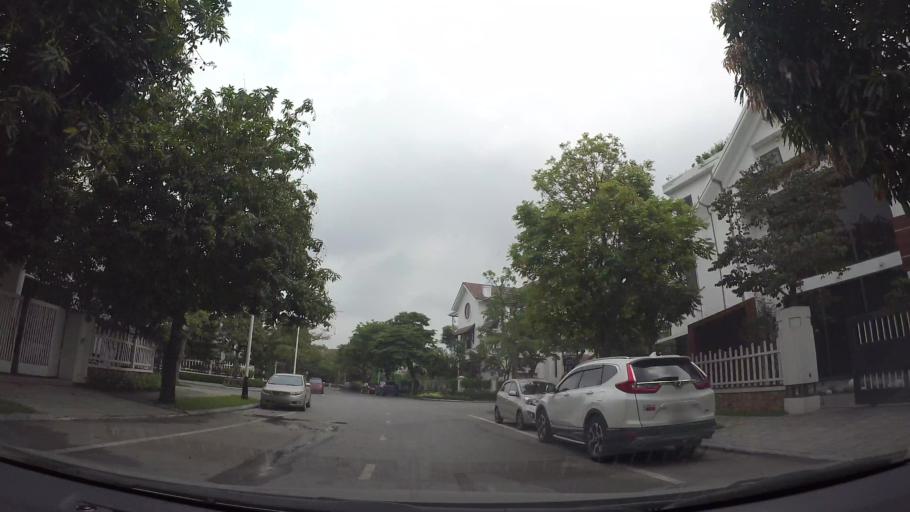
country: VN
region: Ha Noi
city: Trau Quy
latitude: 21.0407
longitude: 105.9211
